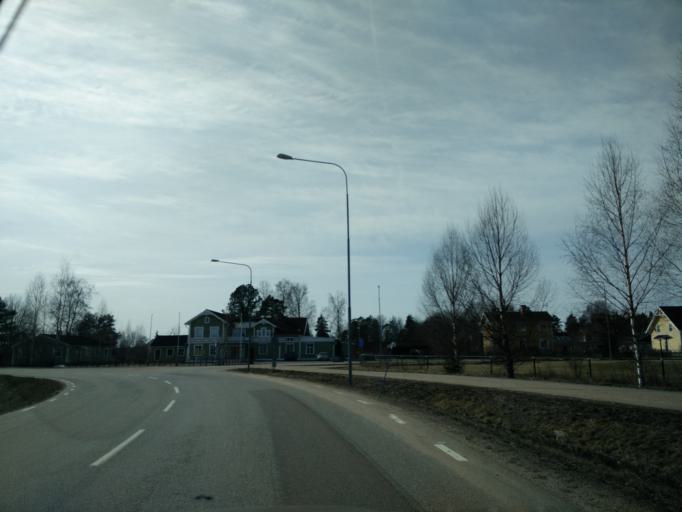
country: SE
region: Vaermland
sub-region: Hagfors Kommun
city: Hagfors
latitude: 60.0086
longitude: 13.5957
